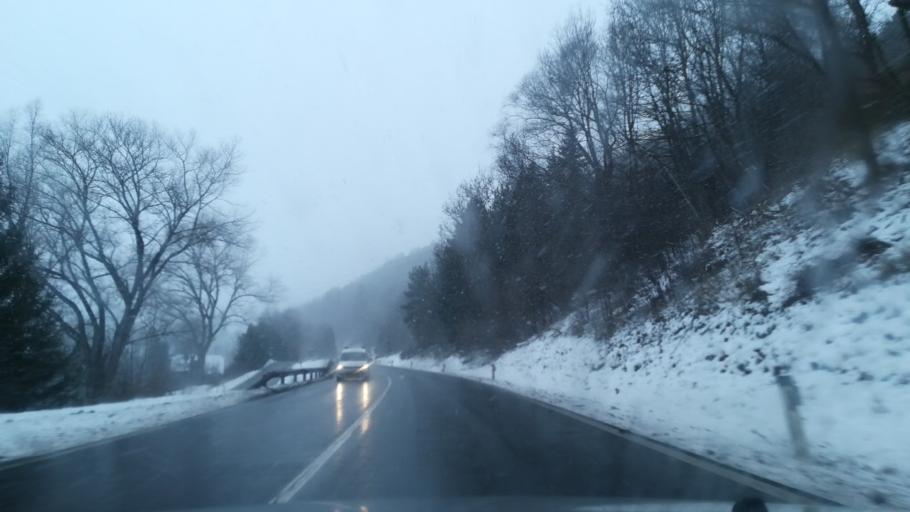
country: AT
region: Styria
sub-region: Politischer Bezirk Murtal
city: Poels
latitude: 47.2050
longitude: 14.5849
